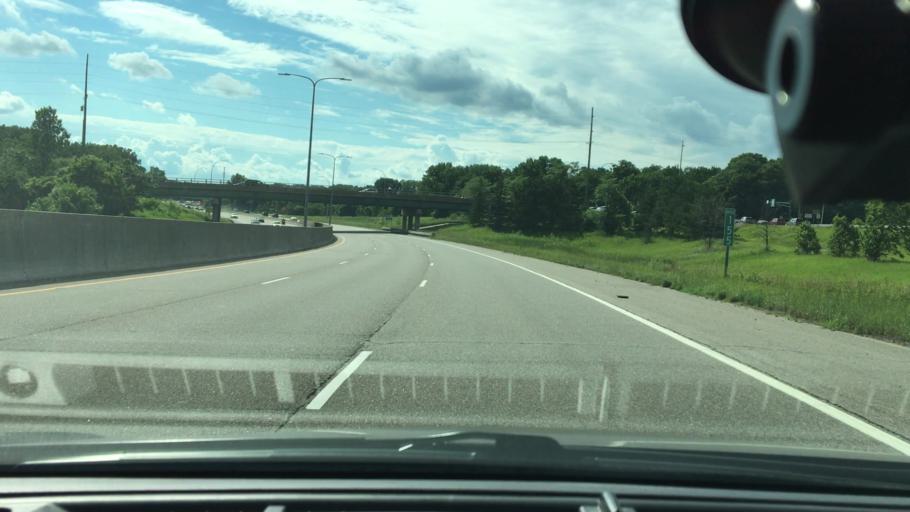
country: US
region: Minnesota
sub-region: Hennepin County
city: Wayzata
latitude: 44.9757
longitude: -93.5000
